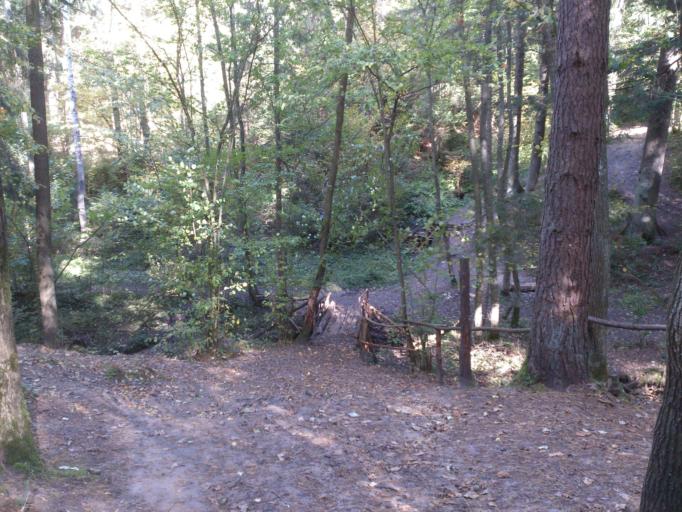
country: LT
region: Kauno apskritis
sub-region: Kaunas
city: Eiguliai
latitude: 54.9388
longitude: 23.9319
